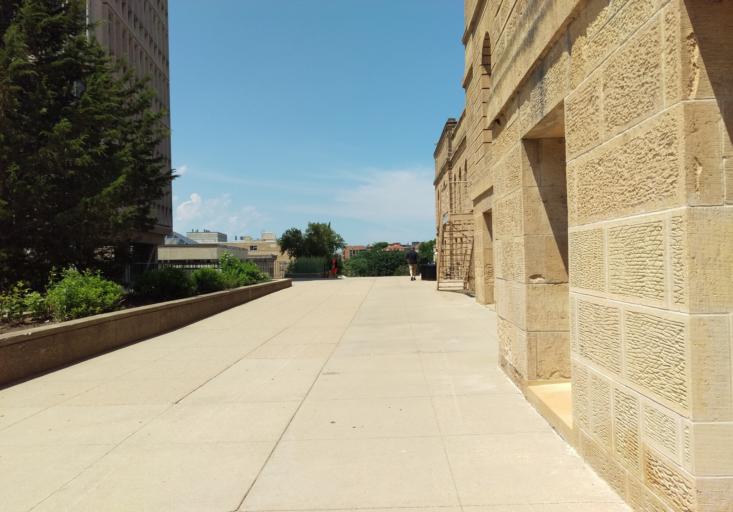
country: US
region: Wisconsin
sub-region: Dane County
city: Madison
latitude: 43.0750
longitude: -89.4042
